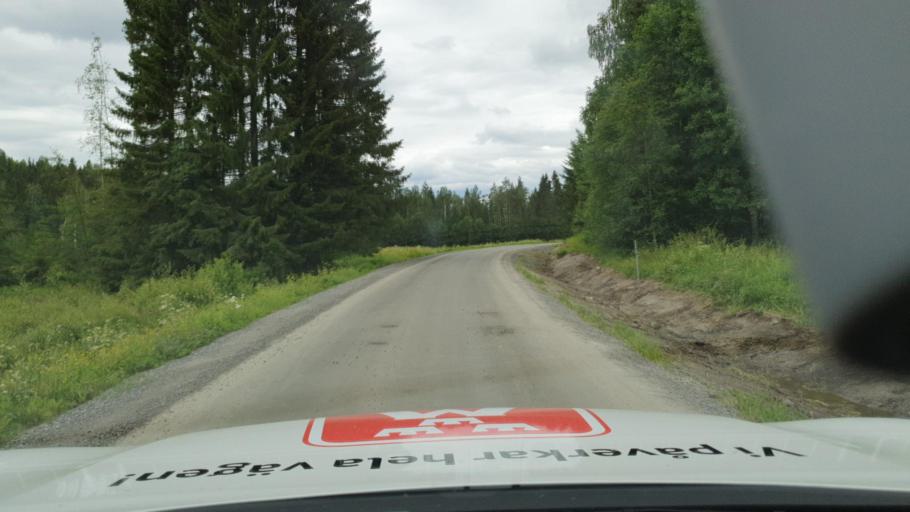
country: SE
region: Vaesterbotten
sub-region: Nordmalings Kommun
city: Nordmaling
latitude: 63.6880
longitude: 19.4458
